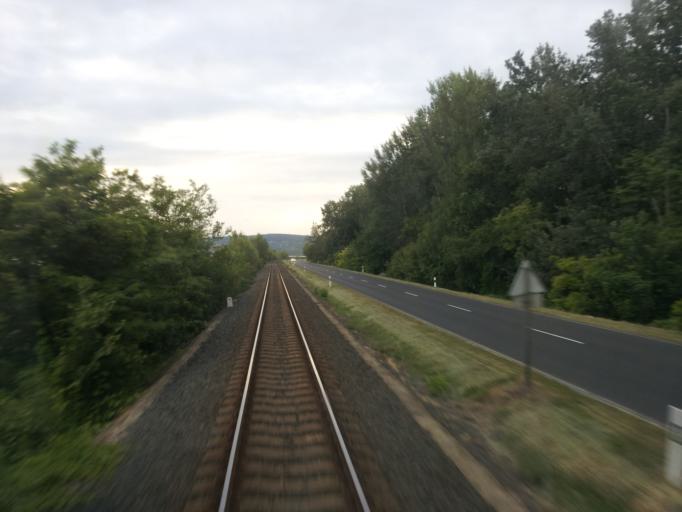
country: HU
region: Veszprem
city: Balatonkenese
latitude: 47.0406
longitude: 18.0683
